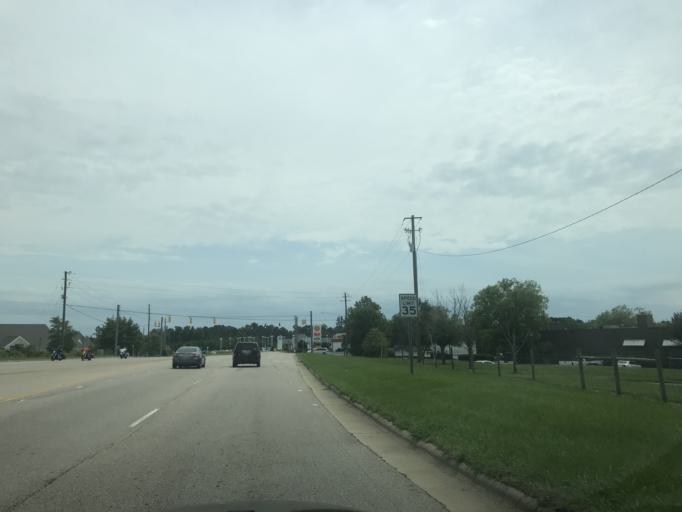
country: US
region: North Carolina
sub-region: Vance County
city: South Henderson
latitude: 36.3256
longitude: -78.4497
